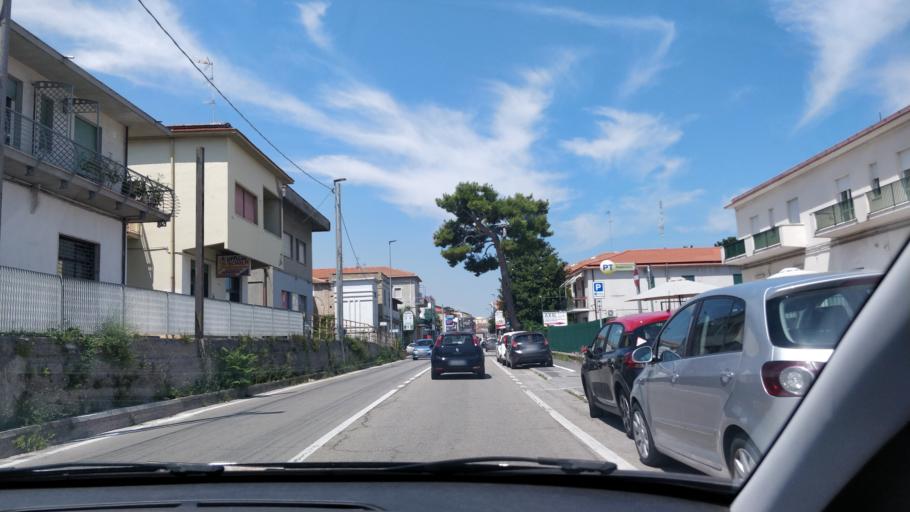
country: IT
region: Abruzzo
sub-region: Provincia di Chieti
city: Francavilla al Mare
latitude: 42.4151
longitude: 14.2984
